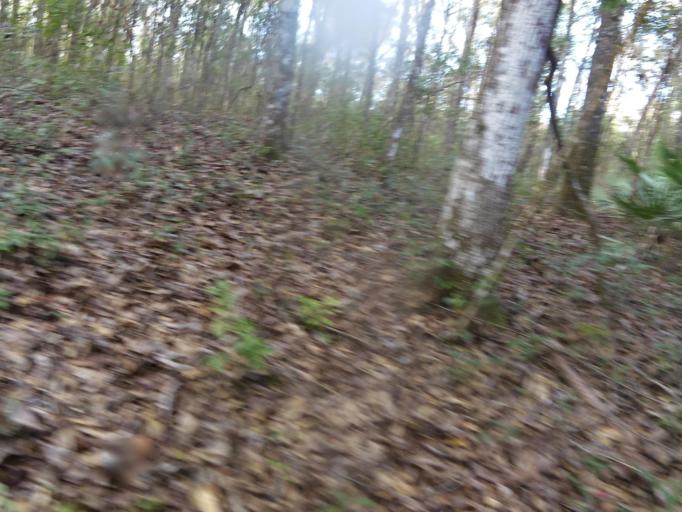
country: US
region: Florida
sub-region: Clay County
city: Middleburg
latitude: 30.1449
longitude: -81.9516
